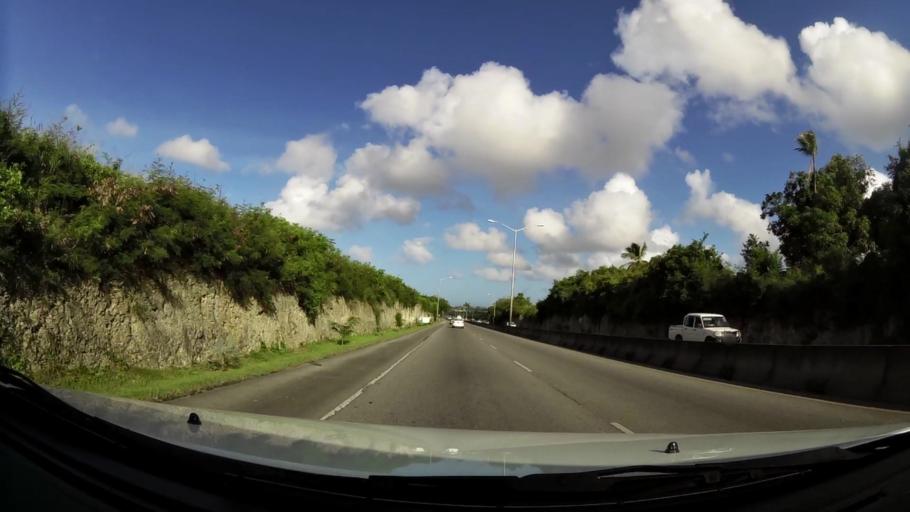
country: BB
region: Saint Michael
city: Bridgetown
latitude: 13.1110
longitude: -59.5813
